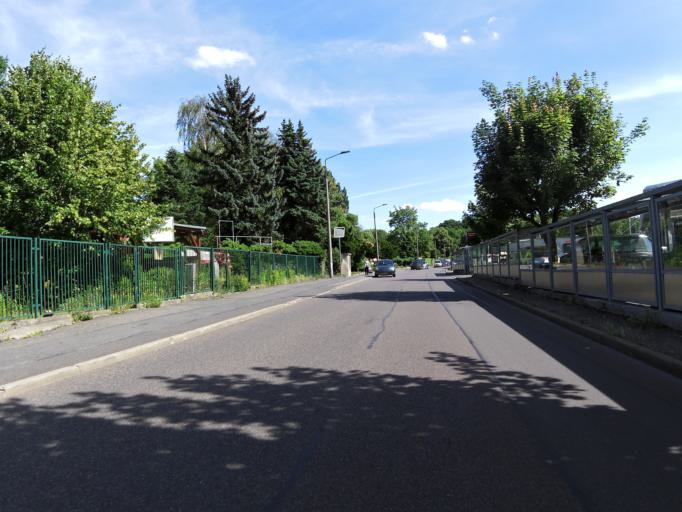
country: DE
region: Saxony
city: Leipzig
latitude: 51.3290
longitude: 12.4176
